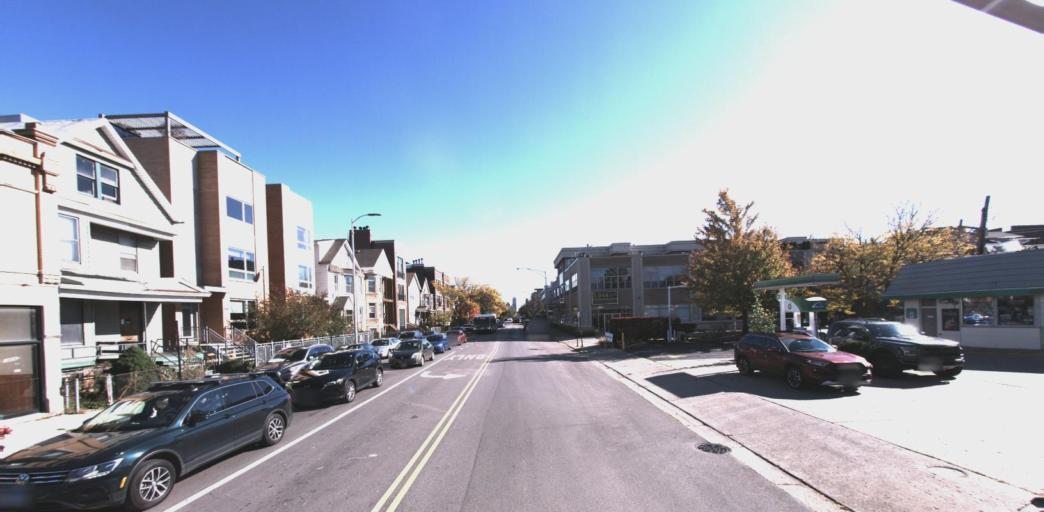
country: US
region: Illinois
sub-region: Cook County
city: Chicago
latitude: 41.9325
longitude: -87.6635
